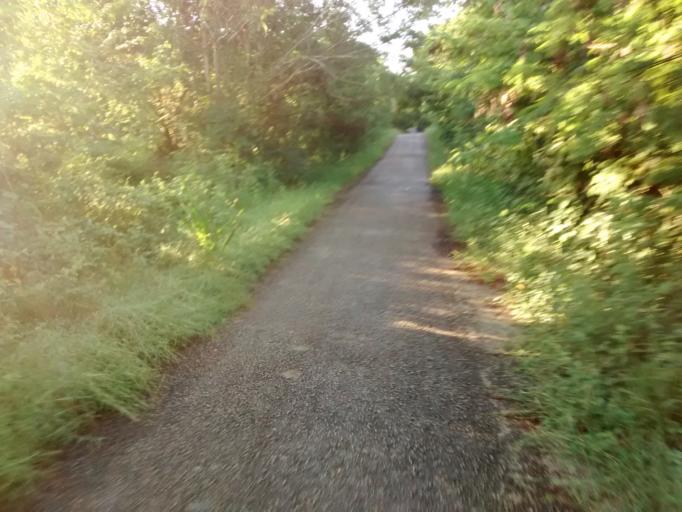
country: MX
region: Yucatan
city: Valladolid
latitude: 20.7218
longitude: -88.2260
